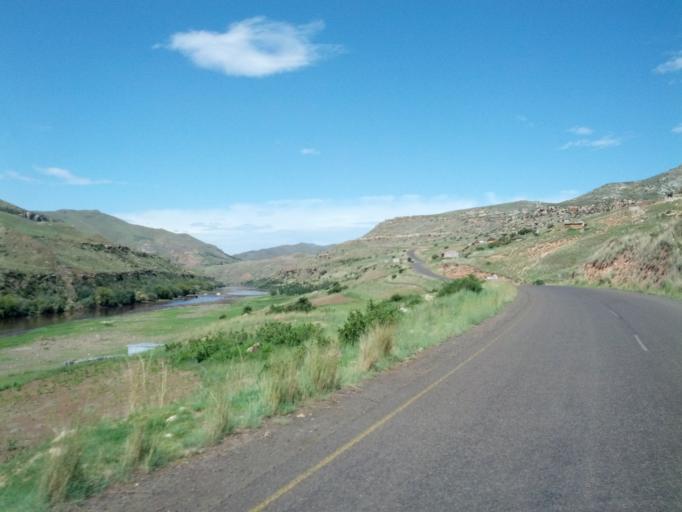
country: LS
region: Qacha's Nek
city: Qacha's Nek
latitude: -30.0628
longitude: 28.5082
